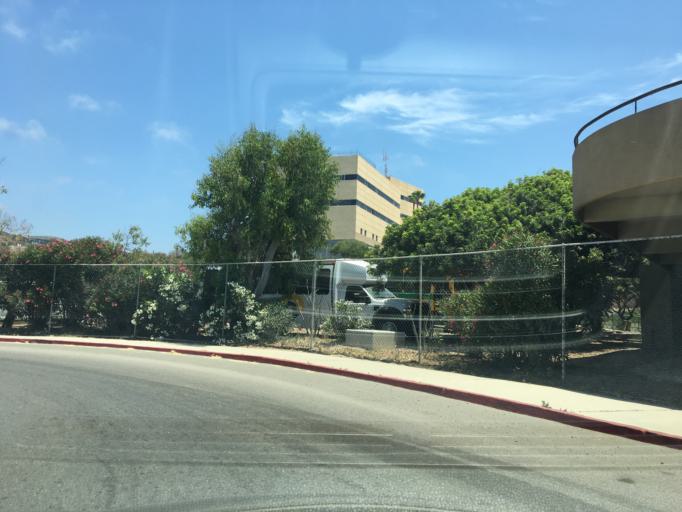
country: MX
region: Baja California
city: El Sauzal
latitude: 31.8649
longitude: -116.6675
